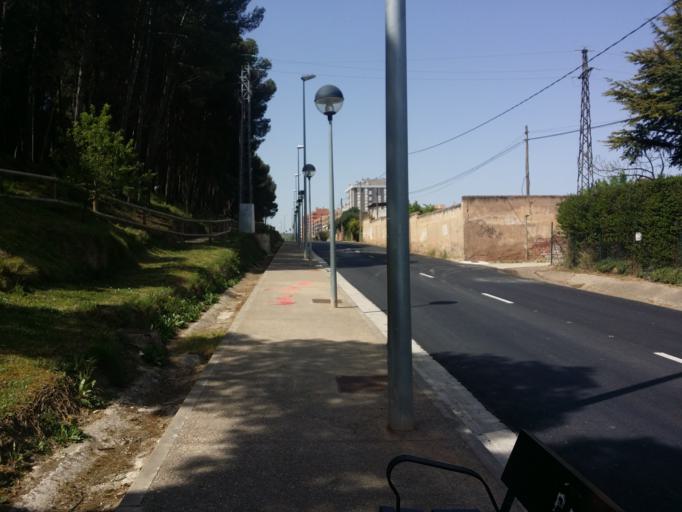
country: ES
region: La Rioja
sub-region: Provincia de La Rioja
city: Logrono
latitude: 42.4679
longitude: -2.4690
